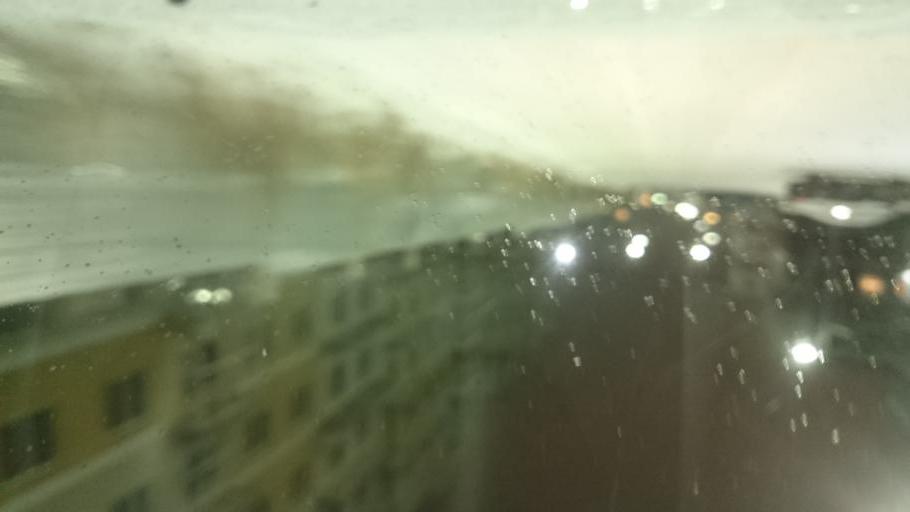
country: RU
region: Tula
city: Barsuki
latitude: 54.1934
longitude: 37.5161
